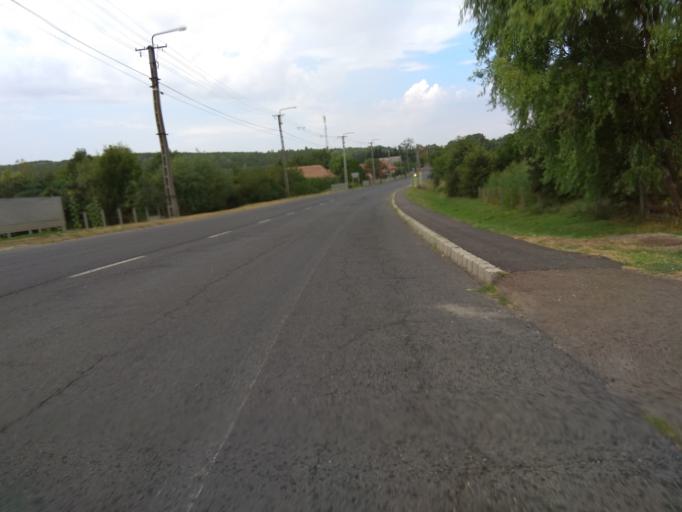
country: HU
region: Borsod-Abauj-Zemplen
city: Harsany
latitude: 47.9212
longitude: 20.7386
